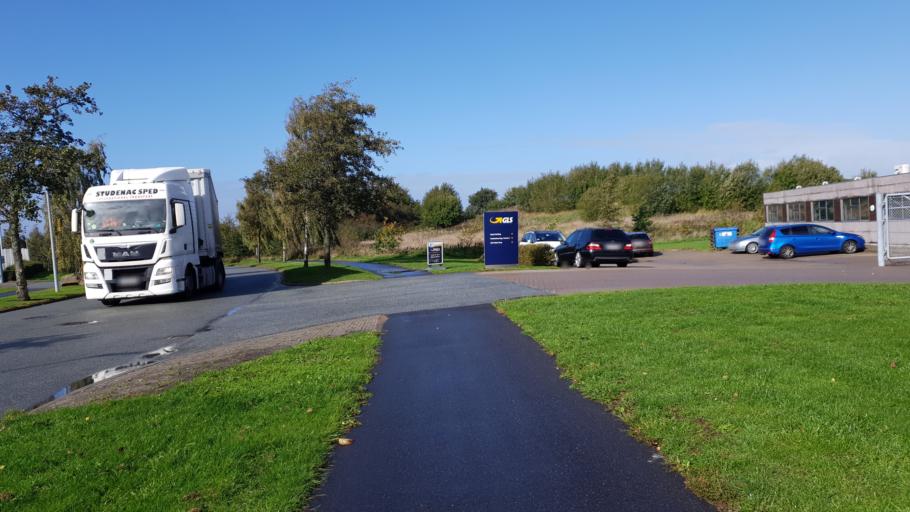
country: DK
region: South Denmark
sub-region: Kolding Kommune
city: Kolding
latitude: 55.5355
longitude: 9.4775
